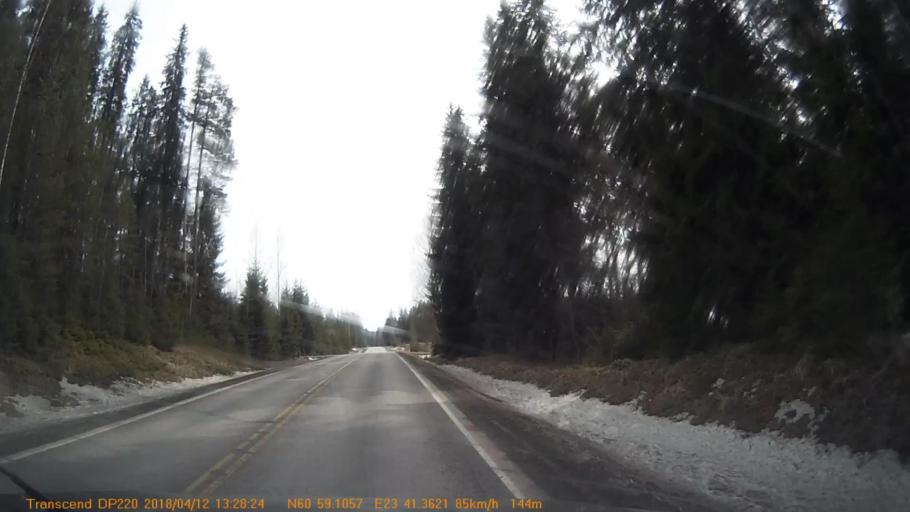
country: FI
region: Pirkanmaa
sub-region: Etelae-Pirkanmaa
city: Kylmaekoski
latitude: 60.9849
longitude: 23.6895
